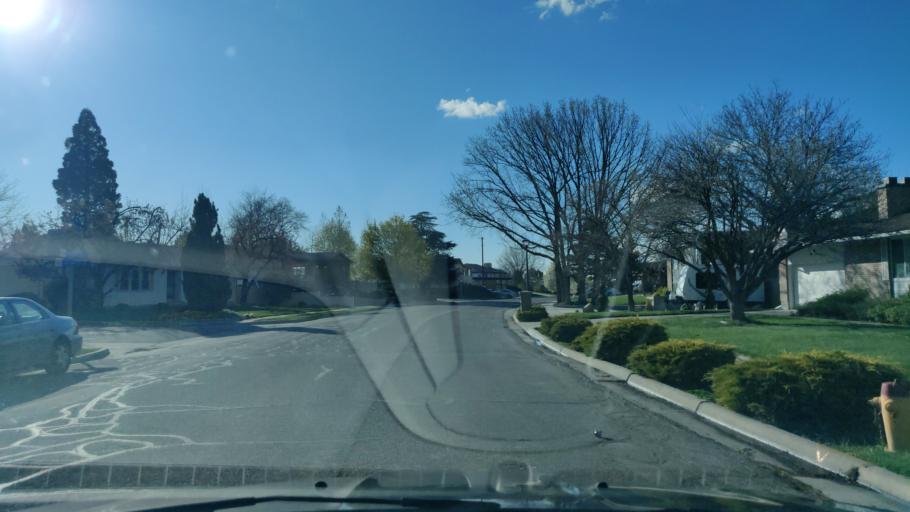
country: US
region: Utah
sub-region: Salt Lake County
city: Cottonwood Heights
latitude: 40.6186
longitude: -111.8189
